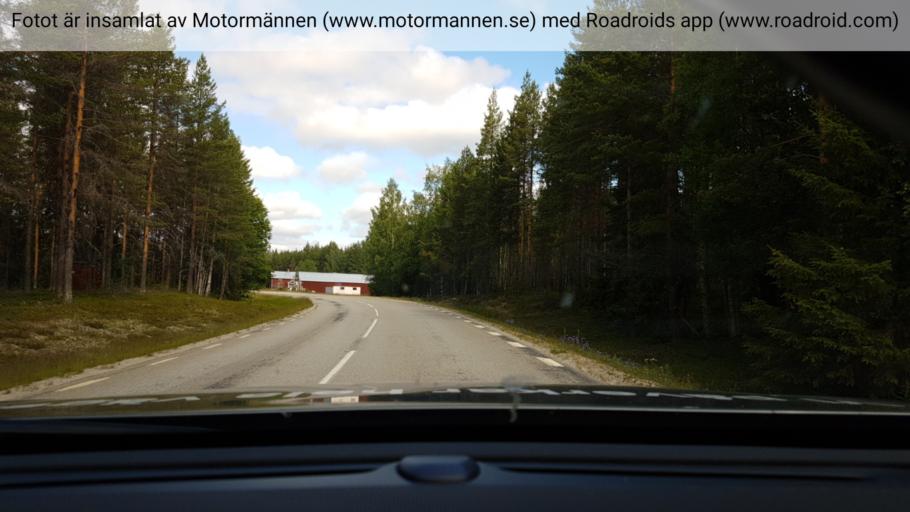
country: SE
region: Vaesterbotten
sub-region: Norsjo Kommun
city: Norsjoe
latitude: 64.7530
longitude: 19.0860
